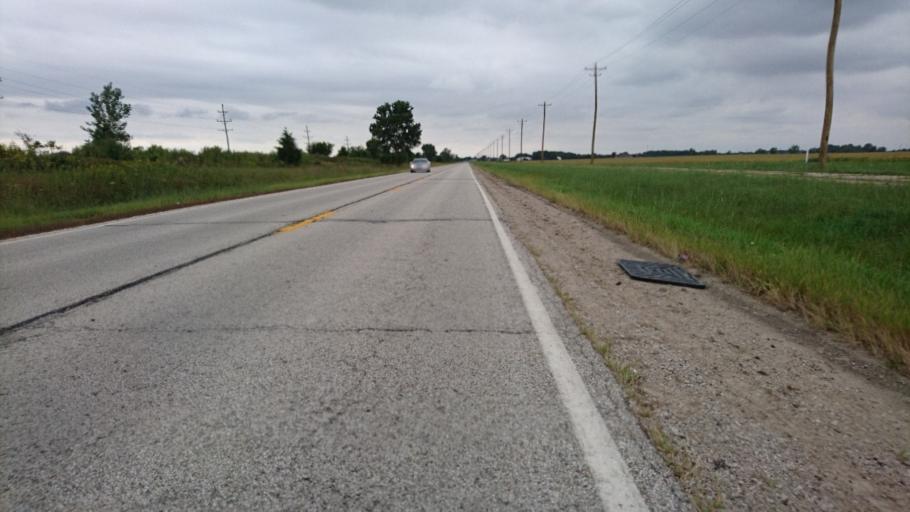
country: US
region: Illinois
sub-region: Livingston County
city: Pontiac
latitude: 40.9106
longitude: -88.6118
